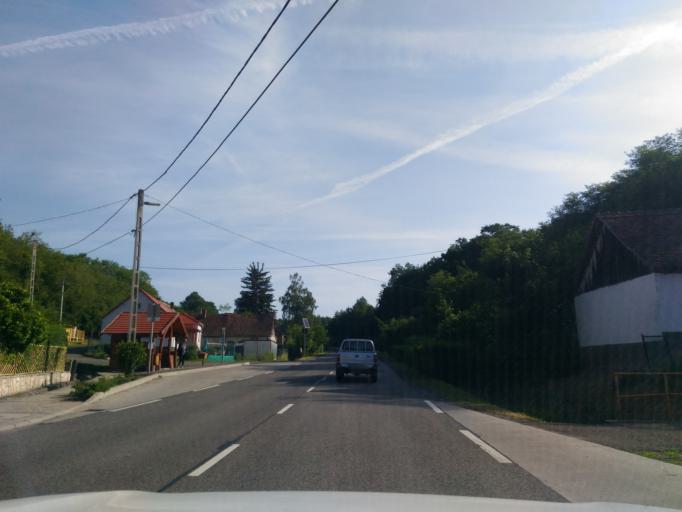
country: HU
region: Baranya
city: Komlo
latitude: 46.1636
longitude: 18.2535
